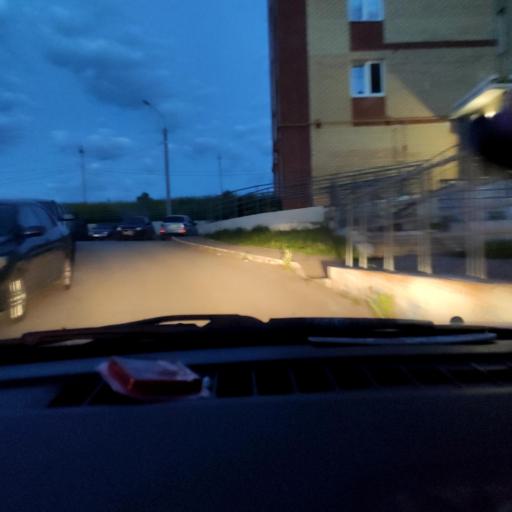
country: RU
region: Perm
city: Lobanovo
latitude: 57.8601
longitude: 56.2895
